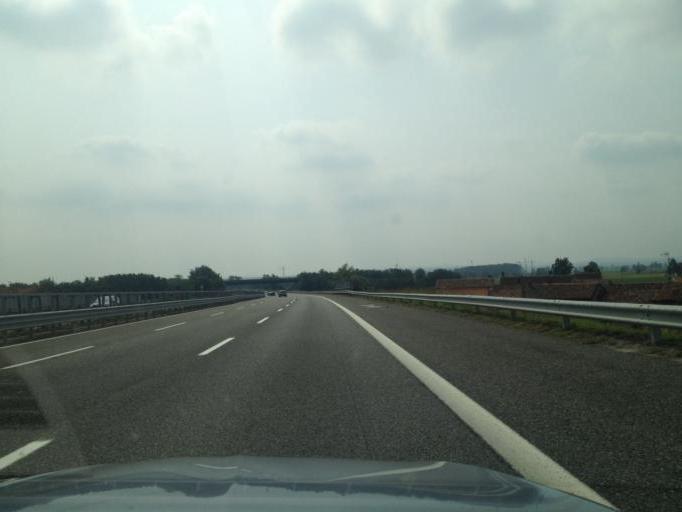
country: IT
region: Piedmont
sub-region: Provincia di Alessandria
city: Borgo San Martino
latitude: 45.1093
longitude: 8.4897
